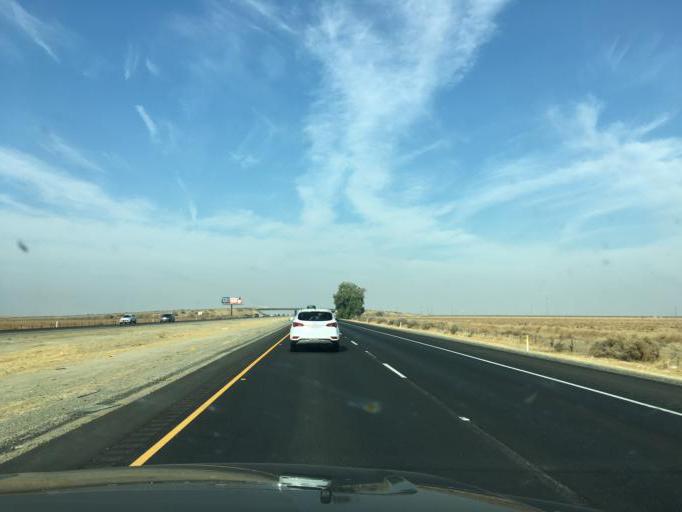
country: US
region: California
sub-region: Kern County
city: Lost Hills
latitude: 35.6620
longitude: -119.6871
